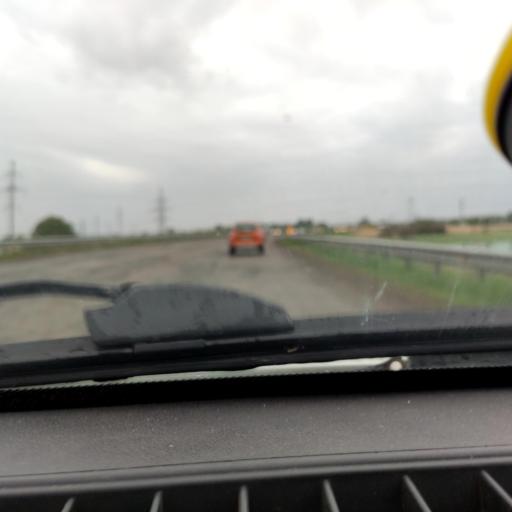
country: RU
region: Samara
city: Tol'yatti
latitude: 53.6715
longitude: 49.4139
